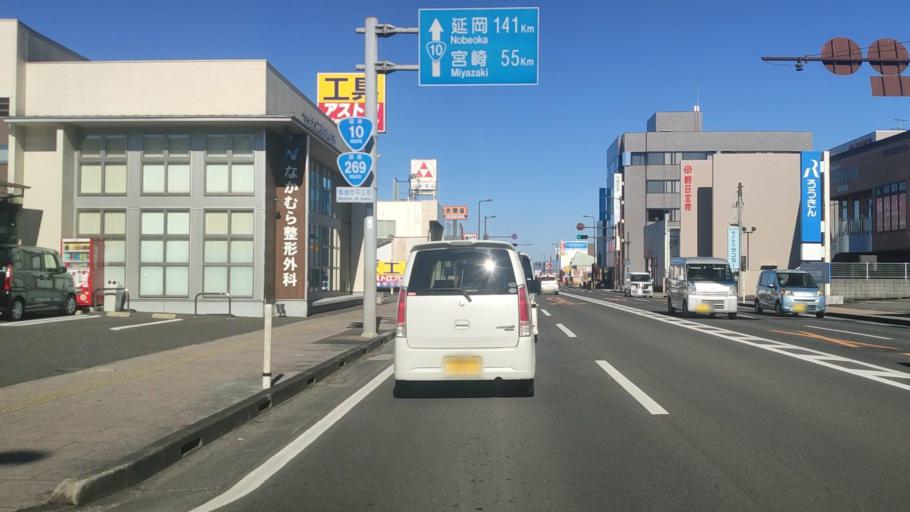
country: JP
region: Miyazaki
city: Miyakonojo
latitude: 31.7328
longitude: 131.0685
